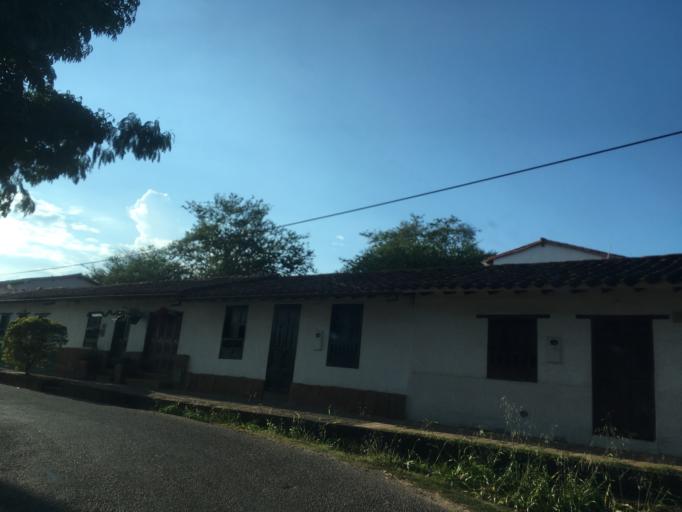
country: CO
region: Santander
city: Barichara
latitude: 6.6350
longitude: -73.2201
